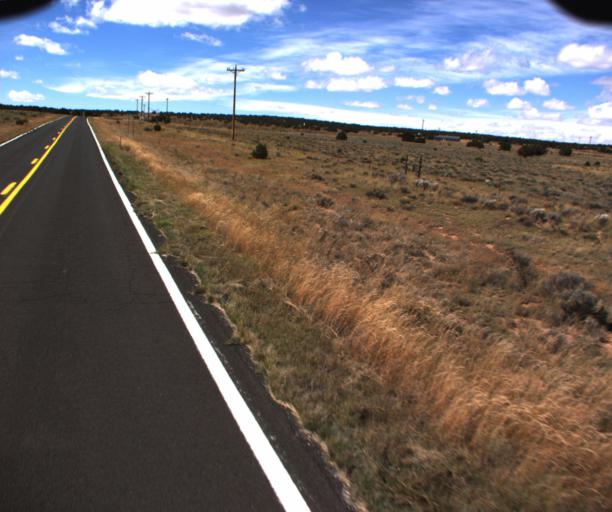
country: US
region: New Mexico
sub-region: McKinley County
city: Zuni Pueblo
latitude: 34.9929
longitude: -109.1013
